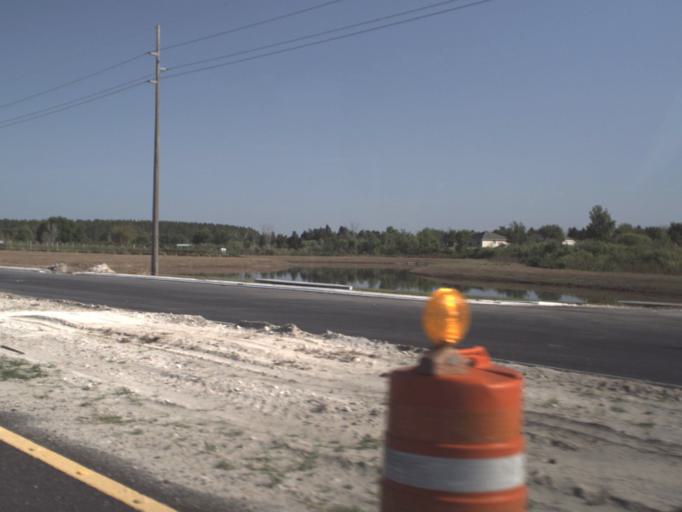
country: US
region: Florida
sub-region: Lake County
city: Four Corners
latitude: 28.4154
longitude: -81.7035
